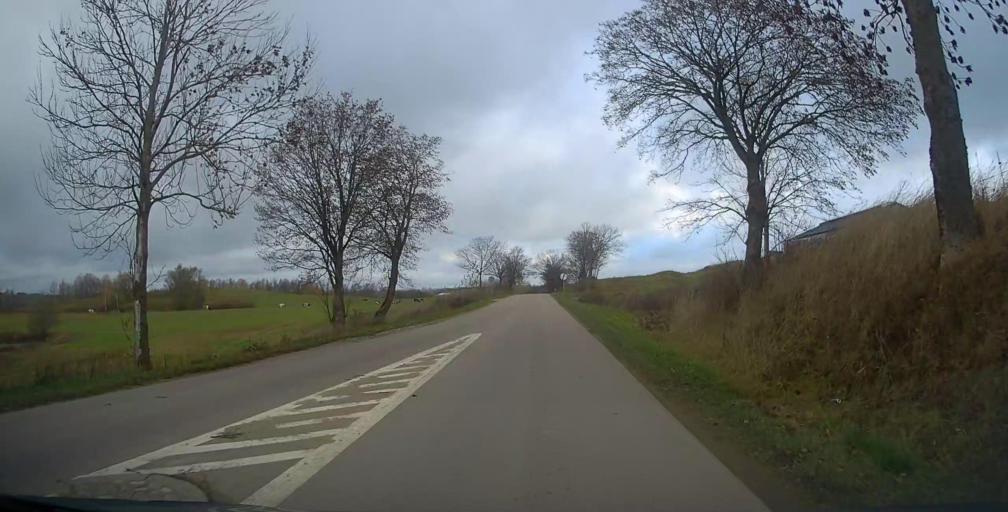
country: PL
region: Podlasie
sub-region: Suwalki
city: Suwalki
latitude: 54.3176
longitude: 22.8637
